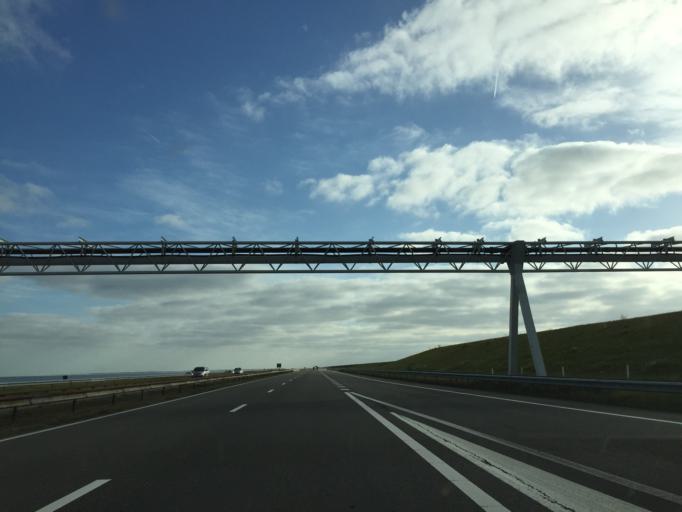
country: NL
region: North Holland
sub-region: Gemeente Hollands Kroon
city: Den Oever
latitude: 53.0187
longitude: 5.2035
